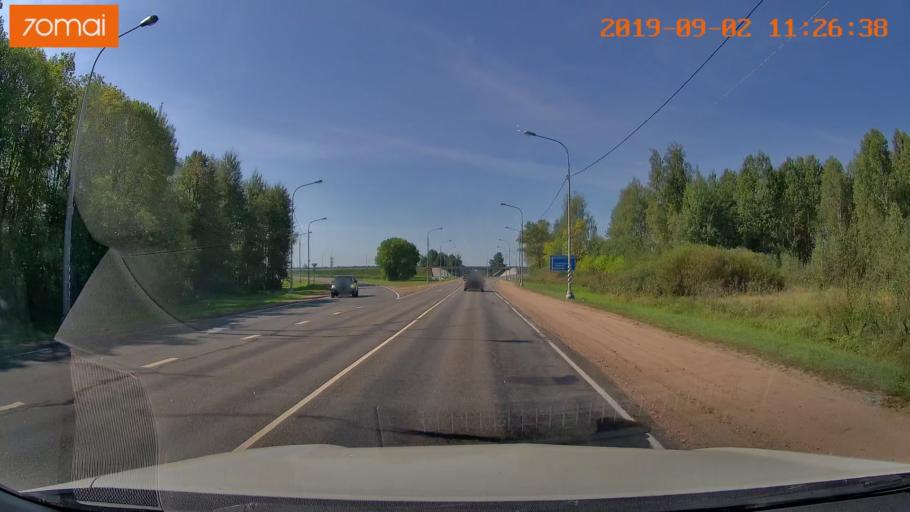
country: RU
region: Smolensk
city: Roslavl'
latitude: 53.9913
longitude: 32.9283
